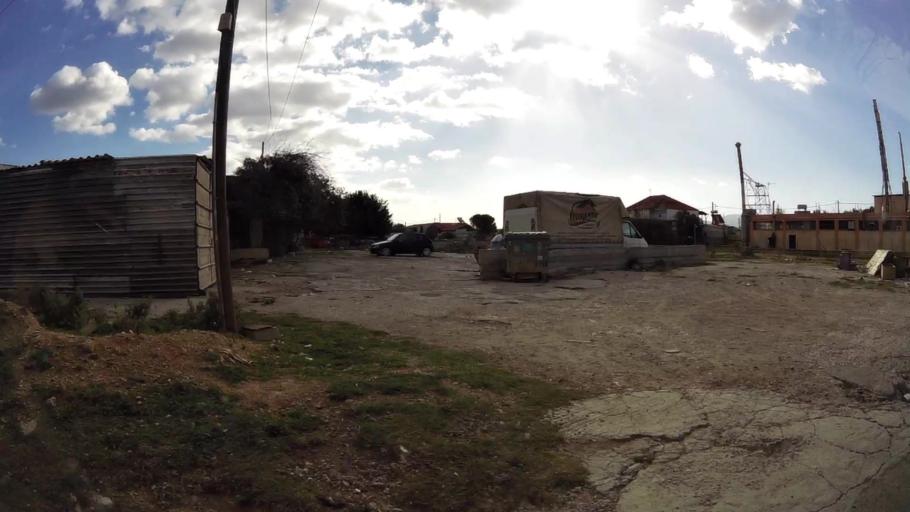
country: GR
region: Attica
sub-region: Nomarchia Anatolikis Attikis
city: Acharnes
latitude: 38.0976
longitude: 23.7516
